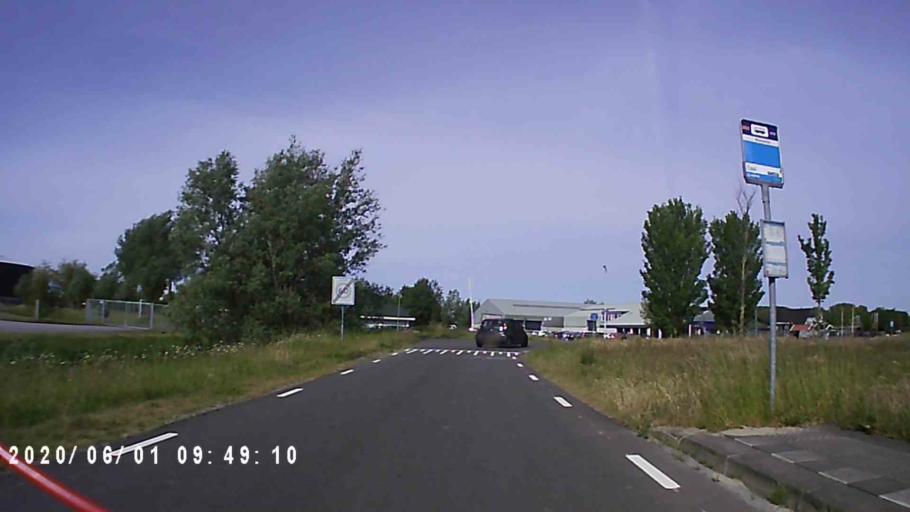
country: NL
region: Friesland
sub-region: Menameradiel
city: Berltsum
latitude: 53.2404
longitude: 5.6682
